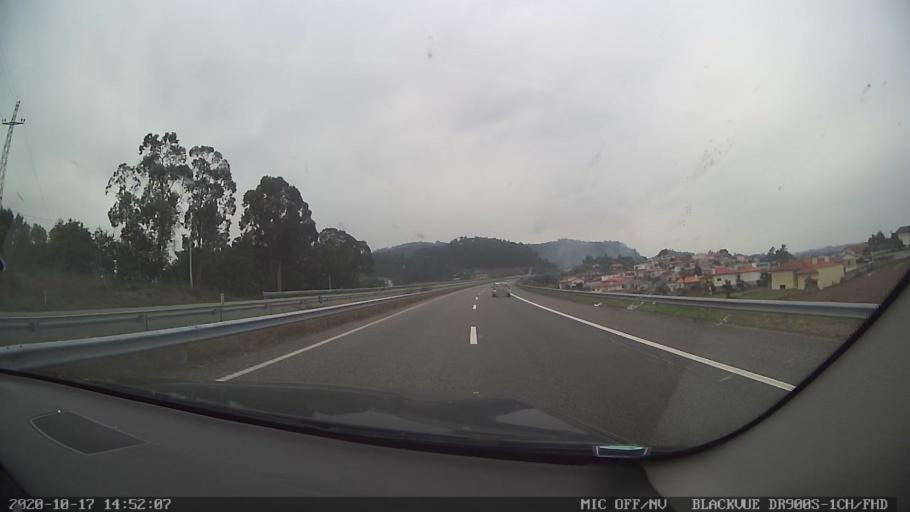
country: PT
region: Braga
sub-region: Barcelos
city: Barcelos
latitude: 41.5055
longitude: -8.6243
